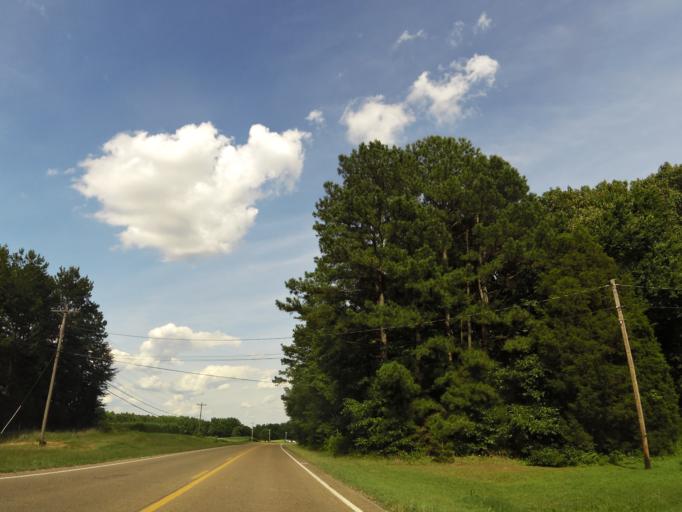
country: US
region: Tennessee
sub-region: Carroll County
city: Bruceton
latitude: 36.0367
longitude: -88.3165
